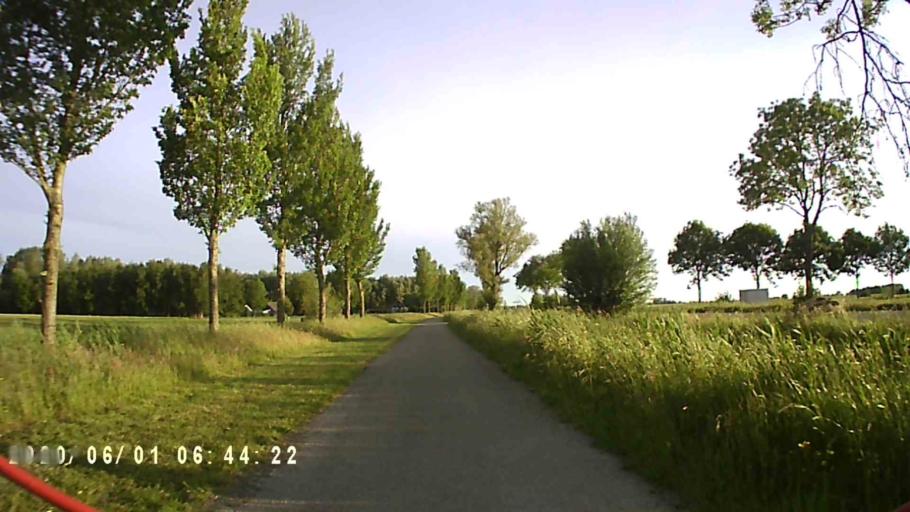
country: NL
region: Friesland
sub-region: Gemeente Kollumerland en Nieuwkruisland
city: Kollum
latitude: 53.3009
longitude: 6.1489
